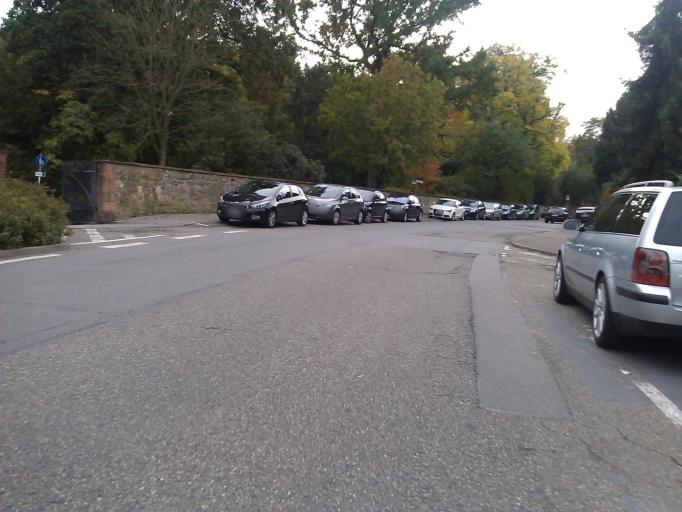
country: DE
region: Baden-Wuerttemberg
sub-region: Karlsruhe Region
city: Weinheim
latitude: 49.5447
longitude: 8.6693
